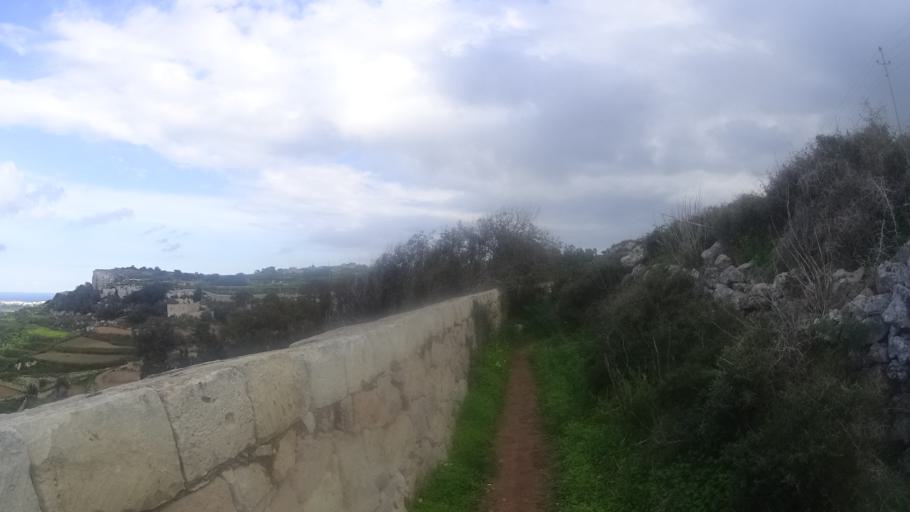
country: MT
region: L-Imgarr
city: Imgarr
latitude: 35.9022
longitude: 14.3660
